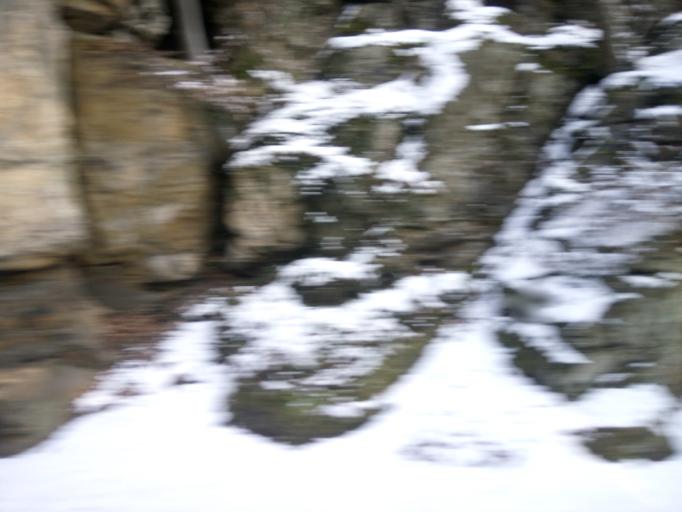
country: LU
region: Grevenmacher
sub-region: Canton d'Echternach
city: Berdorf
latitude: 49.8178
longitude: 6.3737
